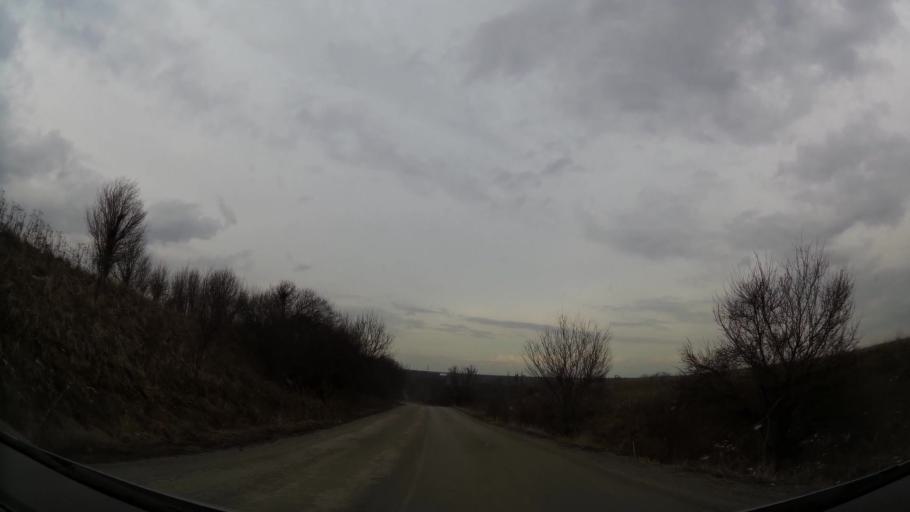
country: BG
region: Sofiya
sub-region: Obshtina Bozhurishte
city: Bozhurishte
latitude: 42.7014
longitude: 23.2207
